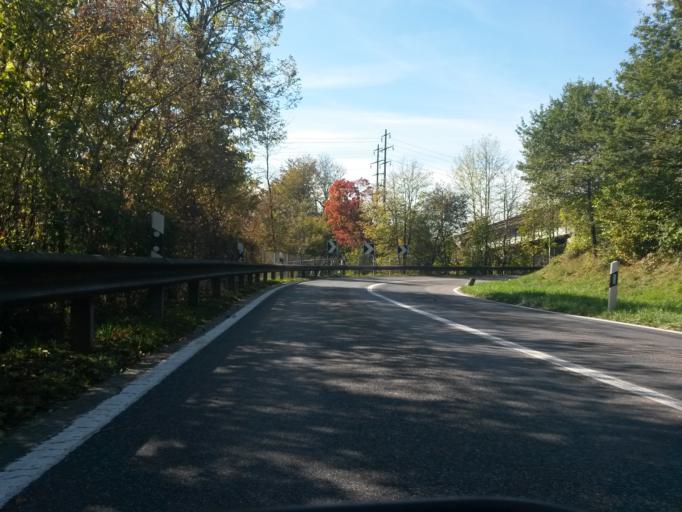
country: CH
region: Bern
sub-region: Oberaargau
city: Wangen an der Aare
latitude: 47.2382
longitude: 7.6677
